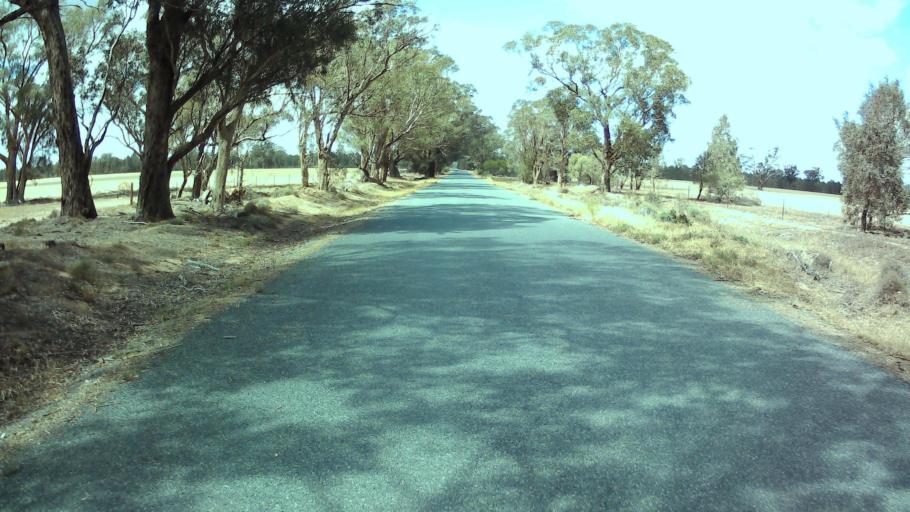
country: AU
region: New South Wales
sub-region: Weddin
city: Grenfell
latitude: -33.8936
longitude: 147.9221
